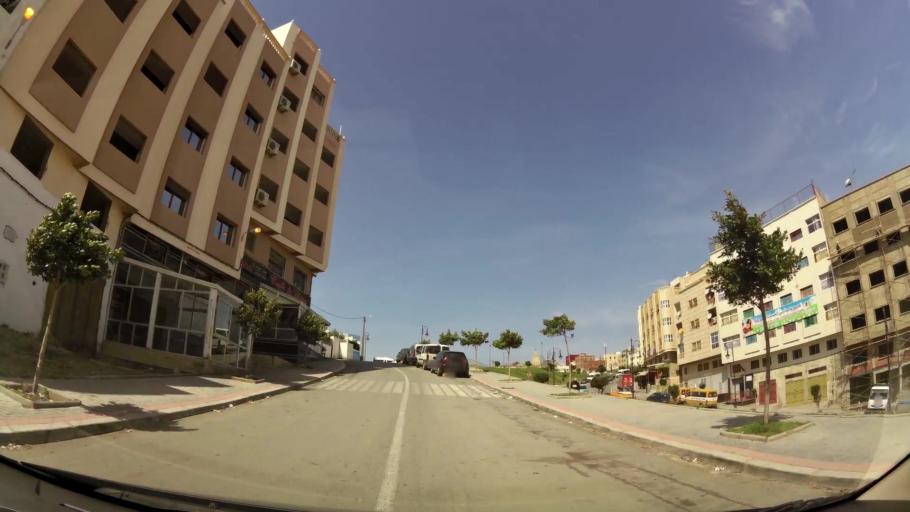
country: MA
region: Tanger-Tetouan
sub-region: Tanger-Assilah
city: Tangier
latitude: 35.7405
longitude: -5.8113
